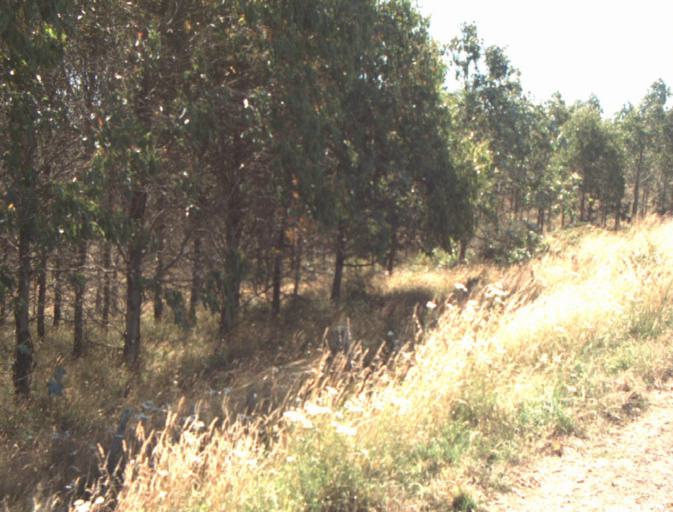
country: AU
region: Tasmania
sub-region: Dorset
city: Scottsdale
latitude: -41.3470
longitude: 147.4540
